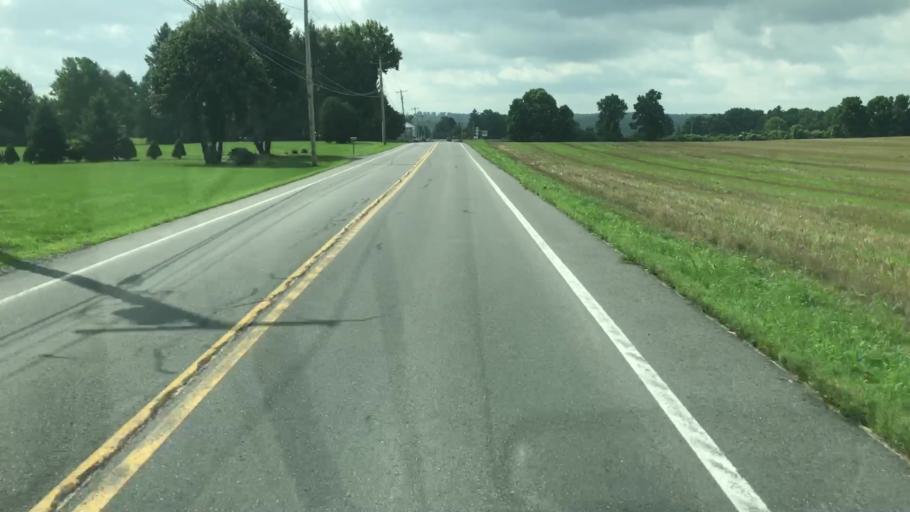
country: US
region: New York
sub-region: Onondaga County
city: Peru
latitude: 43.0393
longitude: -76.3657
